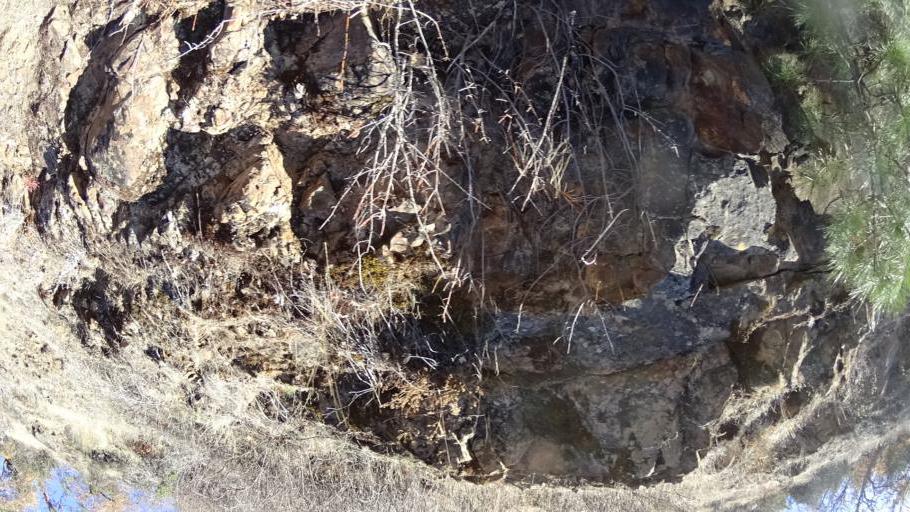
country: US
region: California
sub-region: Siskiyou County
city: Yreka
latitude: 41.8653
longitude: -122.7376
